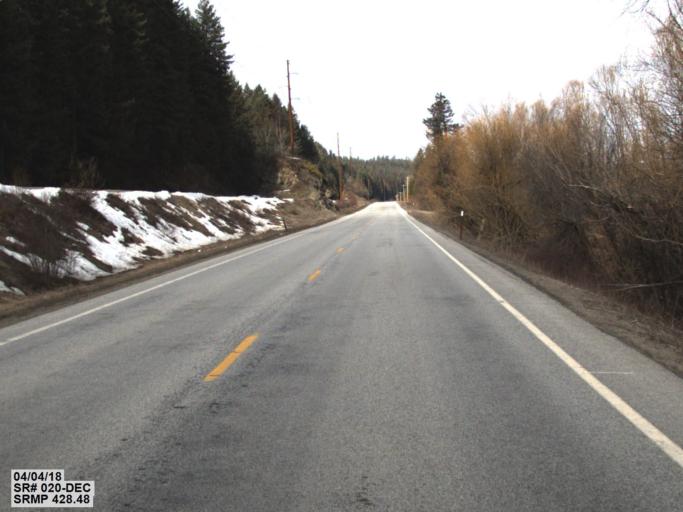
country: US
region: Washington
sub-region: Pend Oreille County
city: Newport
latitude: 48.2308
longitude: -117.1946
